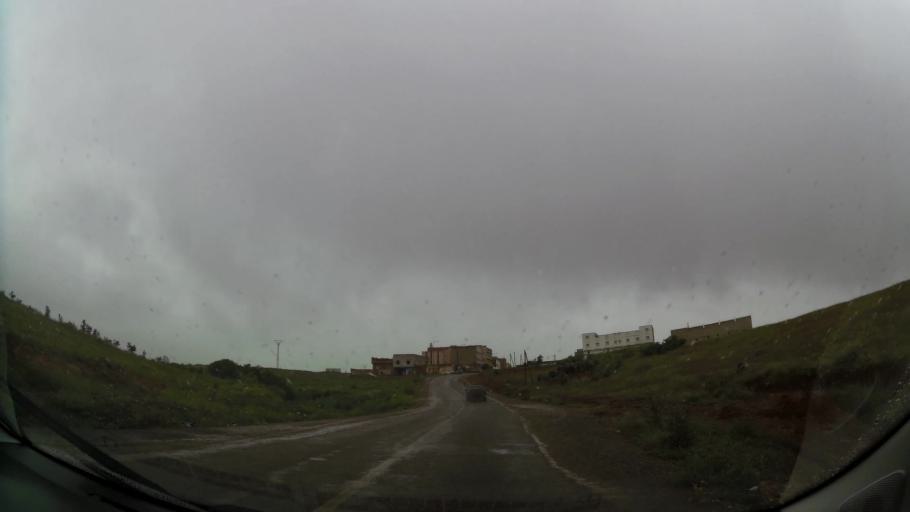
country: MA
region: Oriental
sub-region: Nador
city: Boudinar
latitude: 35.1263
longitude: -3.6289
